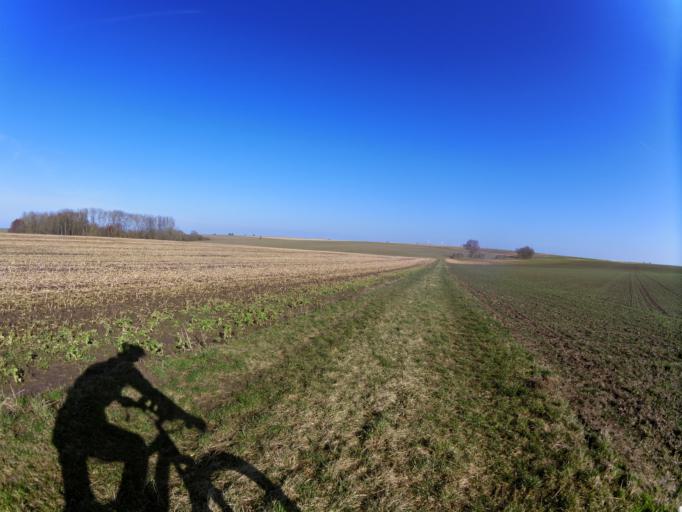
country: DE
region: Bavaria
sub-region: Regierungsbezirk Unterfranken
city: Giebelstadt
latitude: 49.6874
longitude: 9.9643
